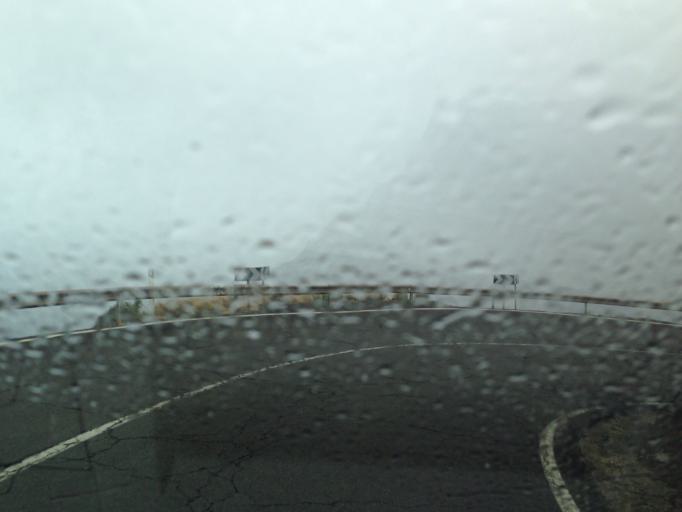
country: ES
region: Canary Islands
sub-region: Provincia de Las Palmas
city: San Nicolas
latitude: 28.0409
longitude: -15.7448
